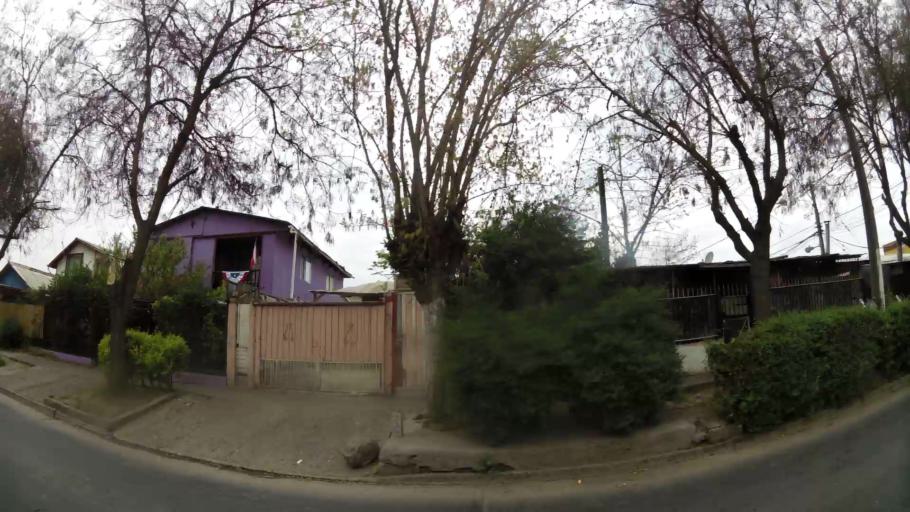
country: CL
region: Santiago Metropolitan
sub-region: Provincia de Santiago
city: Villa Presidente Frei, Nunoa, Santiago, Chile
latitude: -33.4984
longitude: -70.5901
